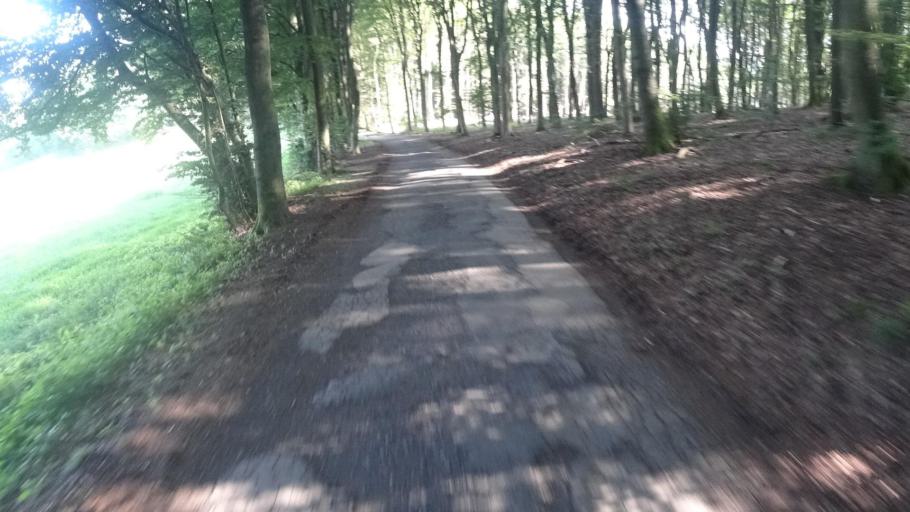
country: DE
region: Rheinland-Pfalz
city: Sankt Katharinen
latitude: 50.5612
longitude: 7.3693
